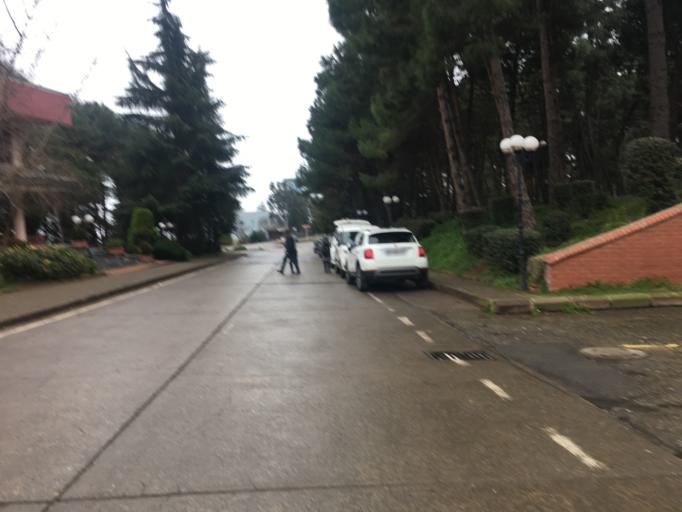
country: TR
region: Trabzon
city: Trabzon
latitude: 40.9968
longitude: 39.7679
